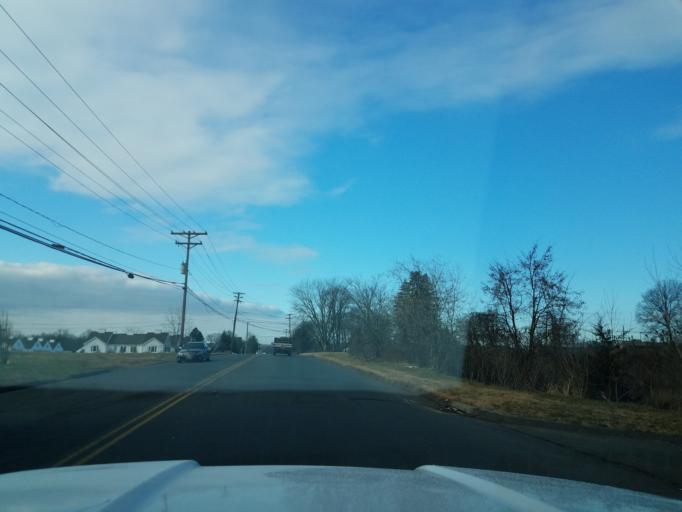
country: US
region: Connecticut
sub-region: Hartford County
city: Kensington
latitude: 41.6411
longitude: -72.7347
